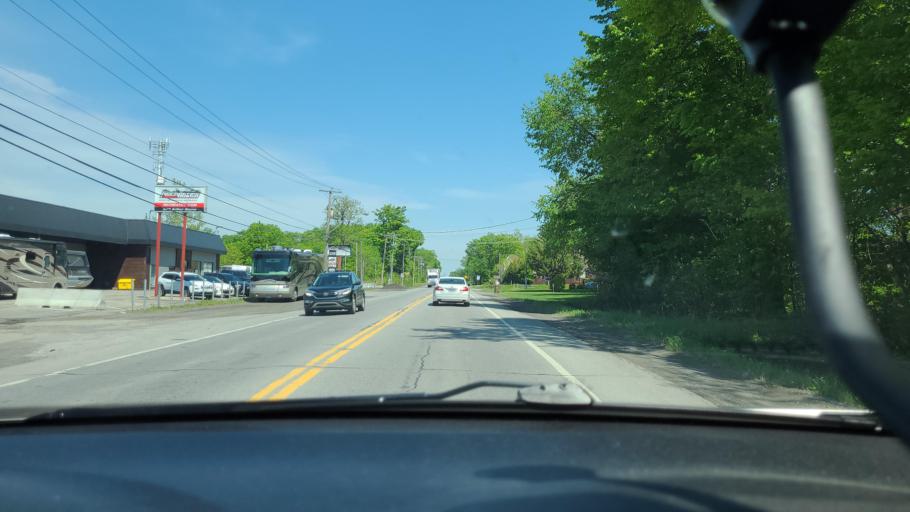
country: CA
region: Quebec
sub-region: Laurentides
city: Saint-Eustache
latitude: 45.5857
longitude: -73.9409
